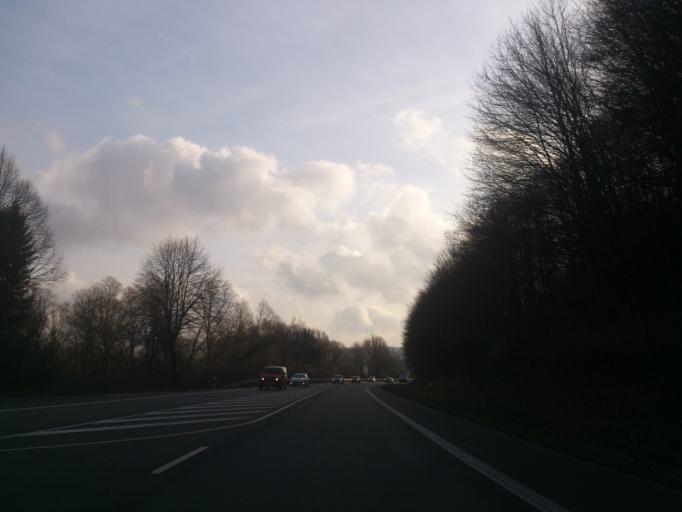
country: DE
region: North Rhine-Westphalia
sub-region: Regierungsbezirk Detmold
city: Bad Driburg
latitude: 51.7203
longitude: 9.0647
